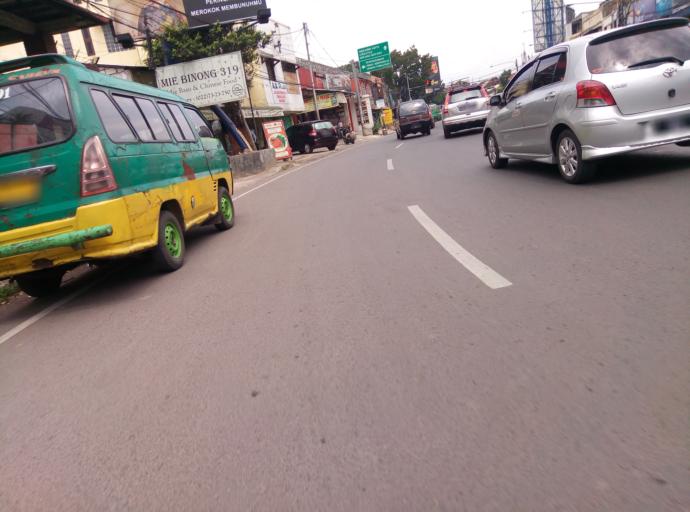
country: ID
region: West Java
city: Bandung
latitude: -6.9309
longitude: 107.6439
